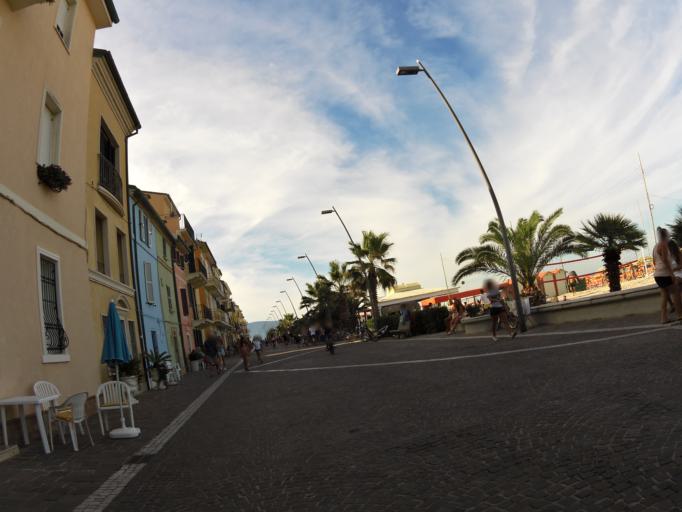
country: IT
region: The Marches
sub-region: Provincia di Macerata
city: Porto Recanati
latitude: 43.4363
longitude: 13.6634
